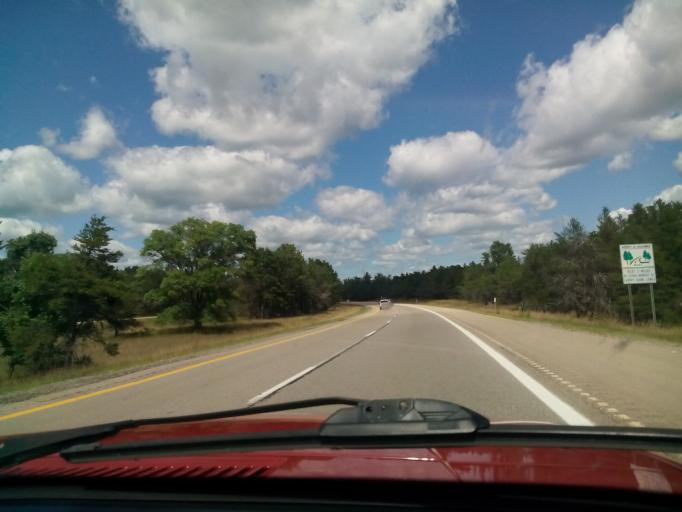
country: US
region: Michigan
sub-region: Crawford County
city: Grayling
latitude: 44.6584
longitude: -84.6984
